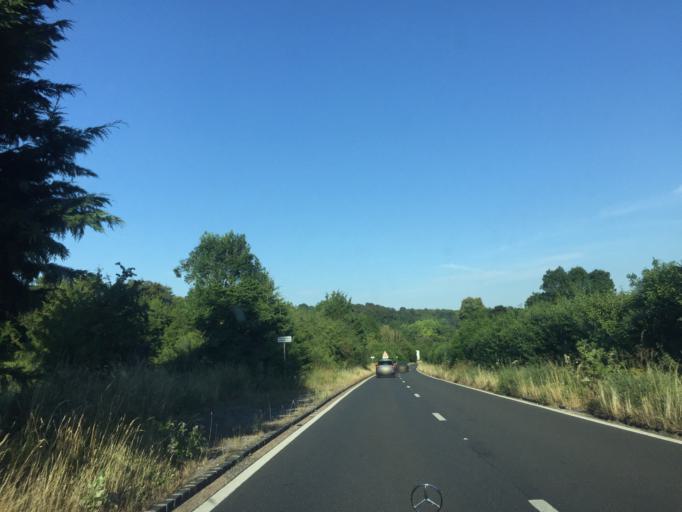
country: GB
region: England
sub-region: Oxfordshire
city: Henley on Thames
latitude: 51.5559
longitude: -0.9342
